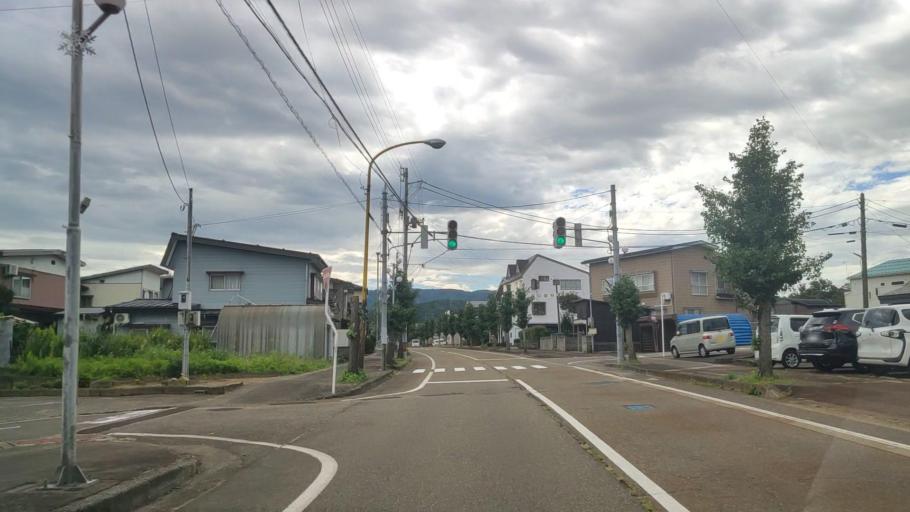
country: JP
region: Niigata
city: Arai
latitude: 37.0216
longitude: 138.2465
